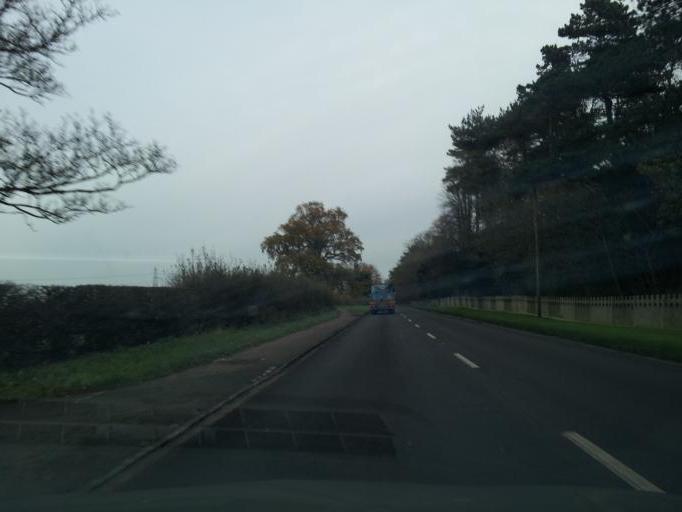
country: GB
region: England
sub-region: Central Bedfordshire
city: Leighton Buzzard
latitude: 51.9012
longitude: -0.7025
